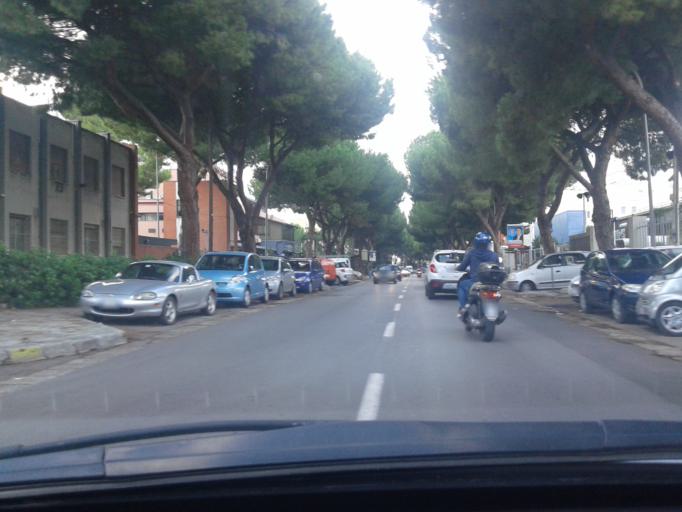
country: IT
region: Sicily
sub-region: Palermo
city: Palermo
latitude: 38.1590
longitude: 13.3168
